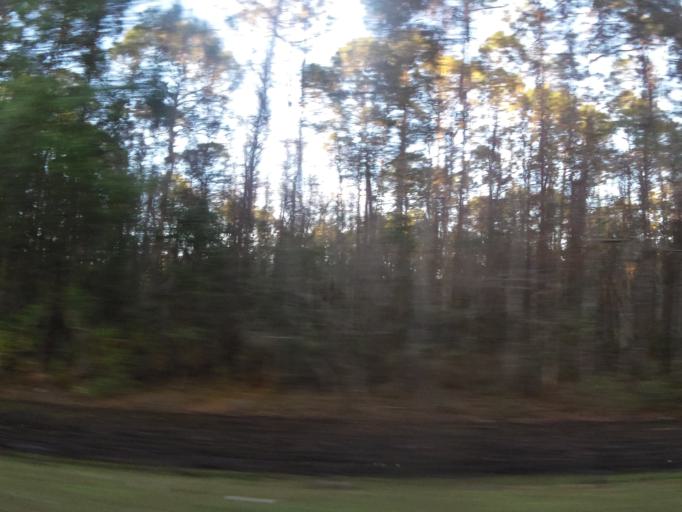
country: US
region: Florida
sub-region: Clay County
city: Green Cove Springs
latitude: 29.8908
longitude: -81.5678
